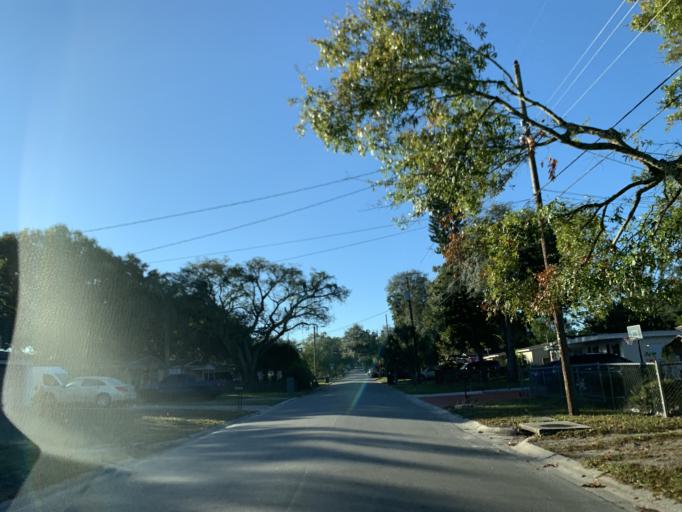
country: US
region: Florida
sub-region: Hillsborough County
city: University
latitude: 28.0428
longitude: -82.4297
